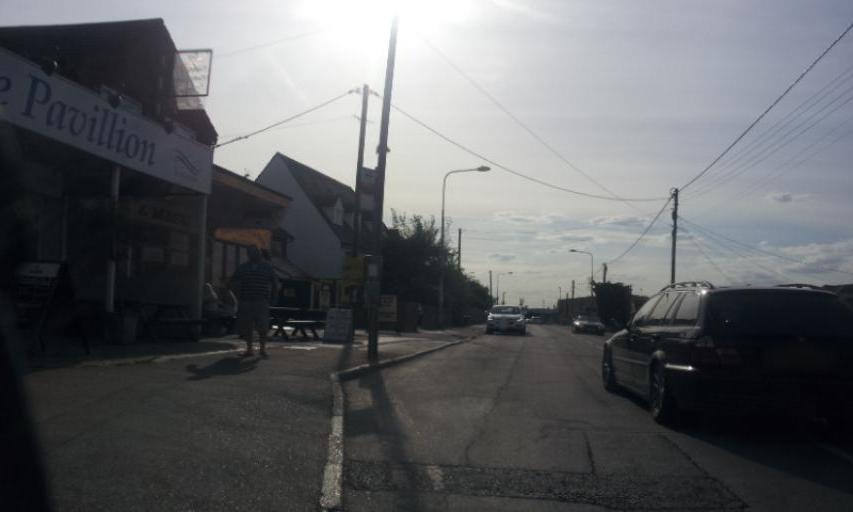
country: GB
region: England
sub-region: Kent
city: Leysdown-on-Sea
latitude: 51.3977
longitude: 0.9204
